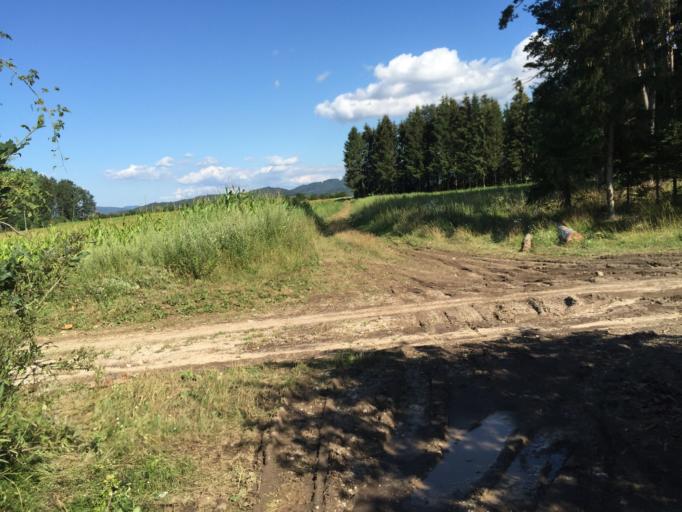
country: AT
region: Carinthia
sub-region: Politischer Bezirk Volkermarkt
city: Feistritz ob Bleiburg
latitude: 46.5627
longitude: 14.7740
